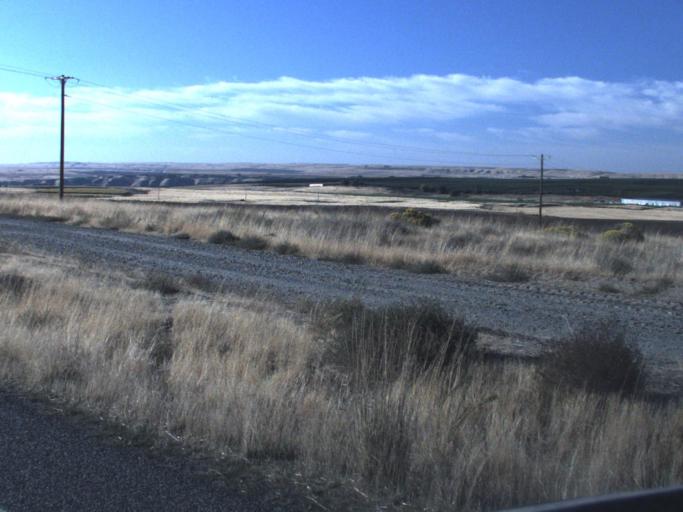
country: US
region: Washington
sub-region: Walla Walla County
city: Burbank
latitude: 46.2978
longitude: -118.7126
